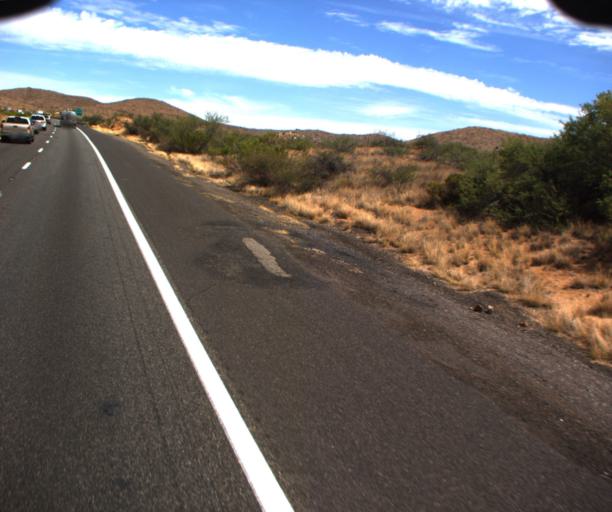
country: US
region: Arizona
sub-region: Yavapai County
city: Cordes Lakes
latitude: 34.2710
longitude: -112.1122
